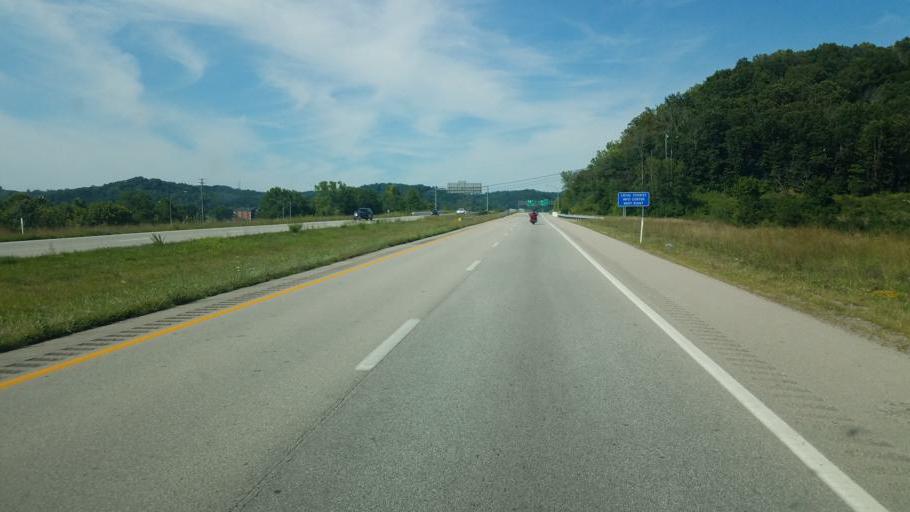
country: US
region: Ohio
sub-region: Athens County
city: Athens
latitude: 39.3237
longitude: -82.0885
